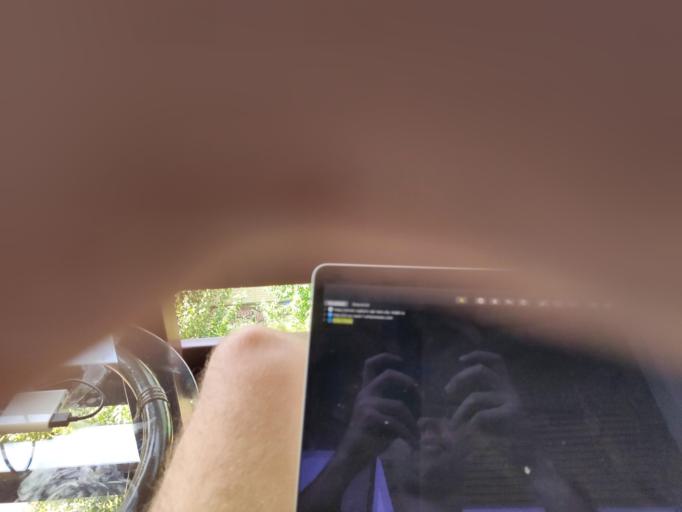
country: RU
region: Krasnodarskiy
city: Vysokoye
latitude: 43.4479
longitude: 40.0256
